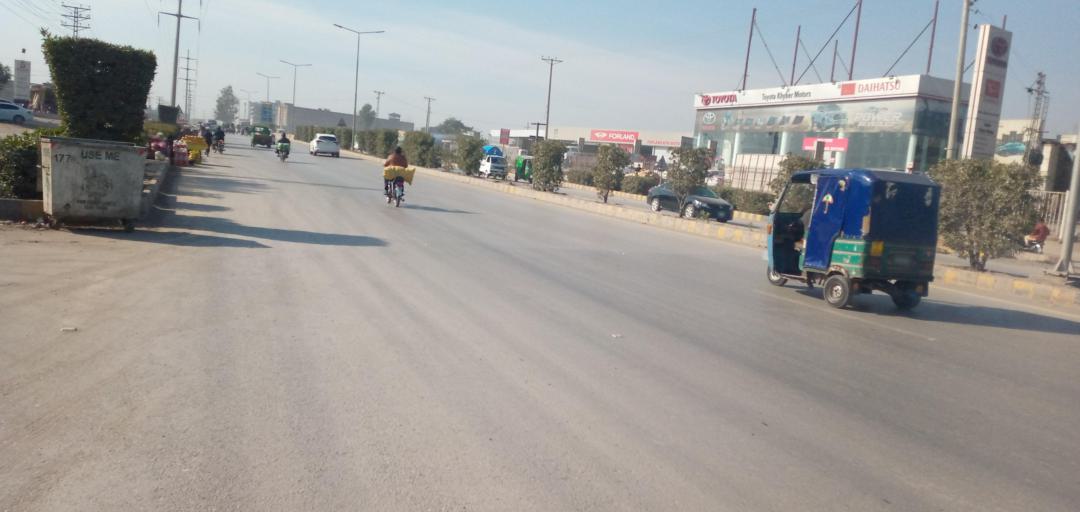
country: PK
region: Khyber Pakhtunkhwa
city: Peshawar
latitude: 33.9698
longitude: 71.5397
